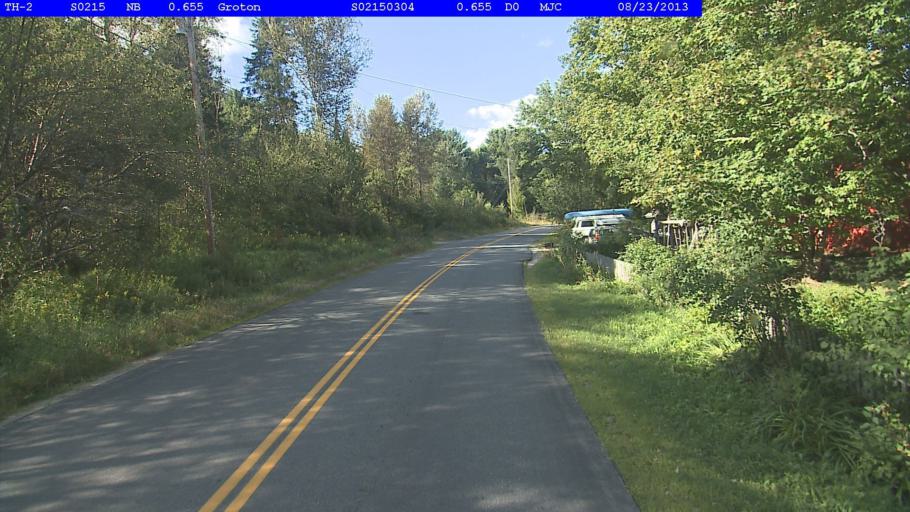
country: US
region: New Hampshire
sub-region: Grafton County
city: Woodsville
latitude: 44.2184
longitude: -72.1918
